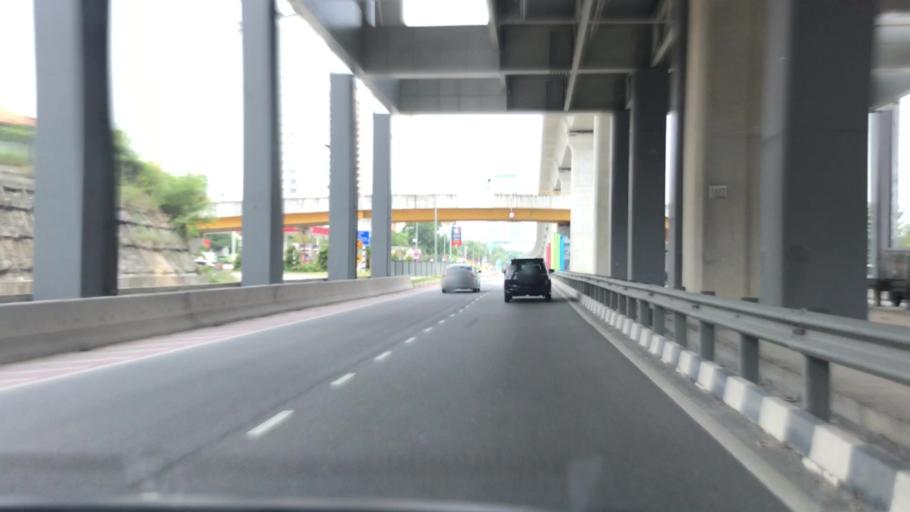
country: MY
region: Selangor
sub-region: Petaling
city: Petaling Jaya
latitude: 3.0546
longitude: 101.6565
